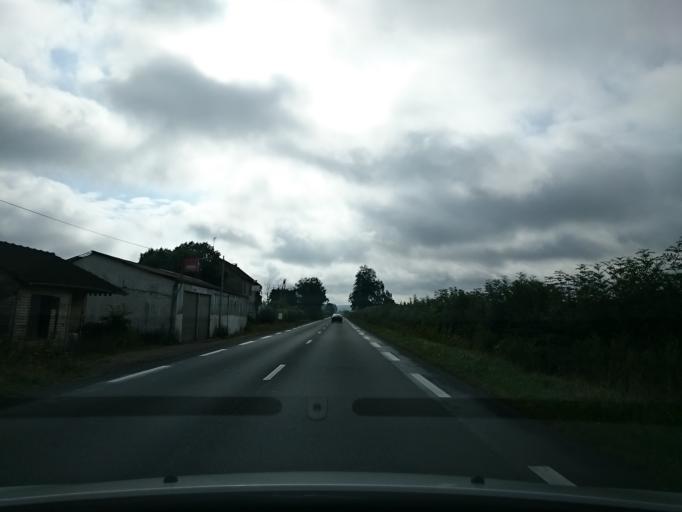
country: FR
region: Lower Normandy
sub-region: Departement du Calvados
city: Cambremer
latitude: 49.1173
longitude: 0.0232
